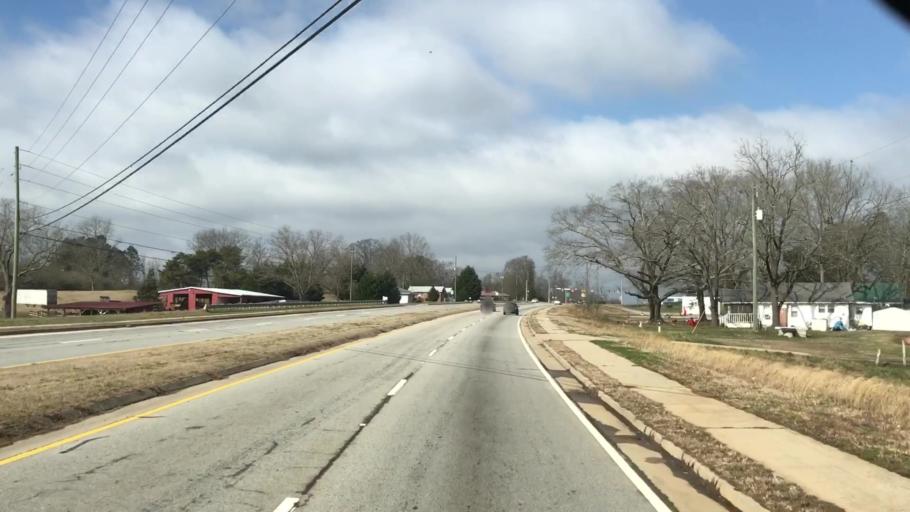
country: US
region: Georgia
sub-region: Hall County
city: Oakwood
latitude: 34.1699
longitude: -83.8360
